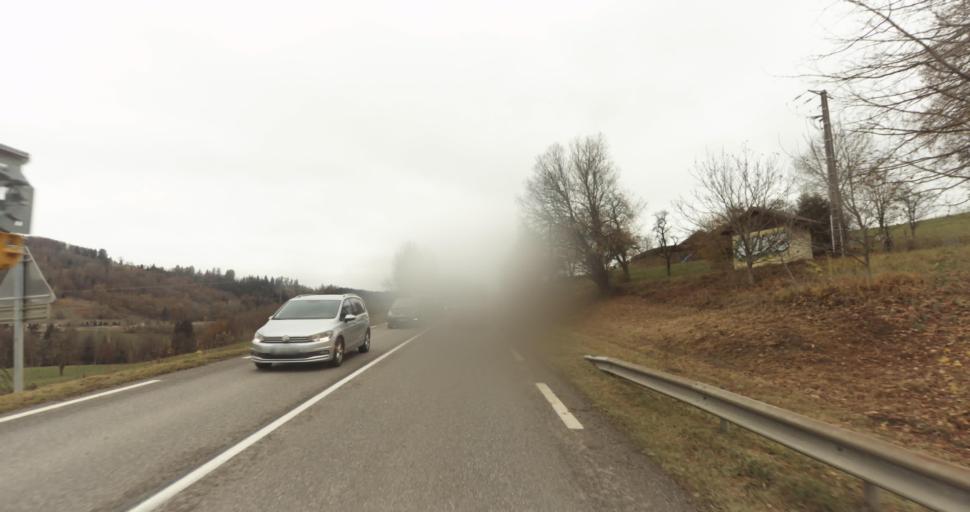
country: FR
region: Rhone-Alpes
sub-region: Departement de la Haute-Savoie
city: Evires
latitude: 46.0267
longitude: 6.2377
